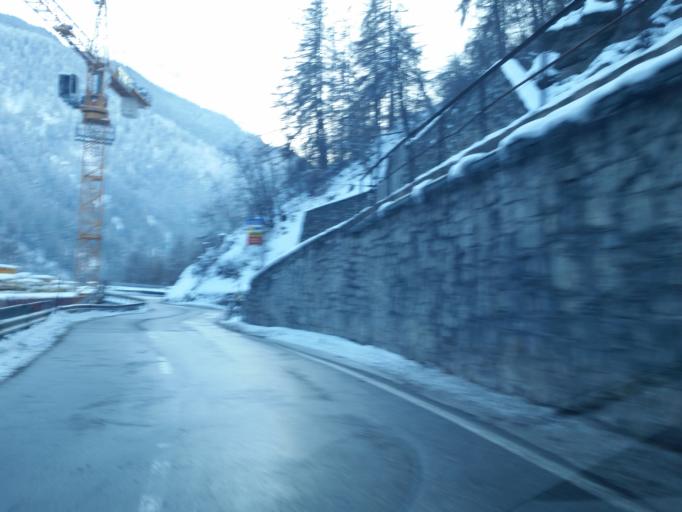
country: CH
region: Grisons
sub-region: Inn District
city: Zernez
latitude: 46.7727
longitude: 10.1602
